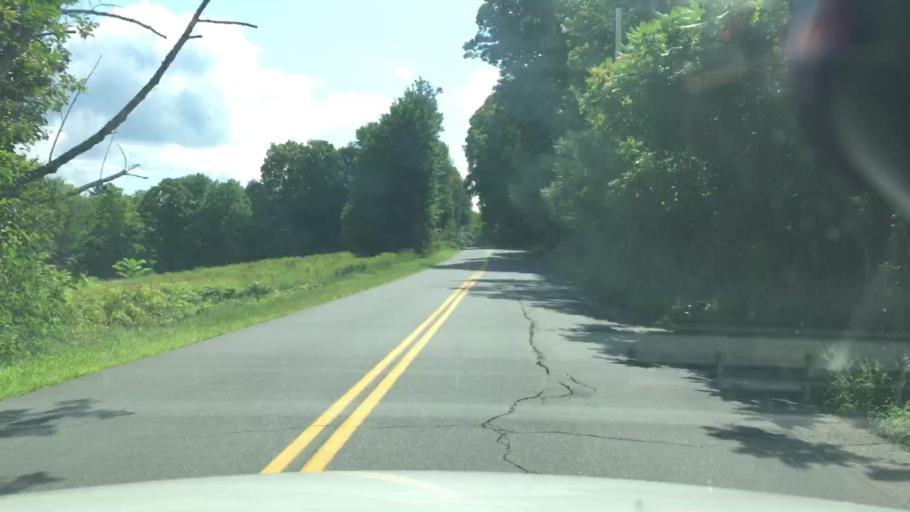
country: US
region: Maine
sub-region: Somerset County
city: Skowhegan
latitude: 44.7337
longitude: -69.7100
